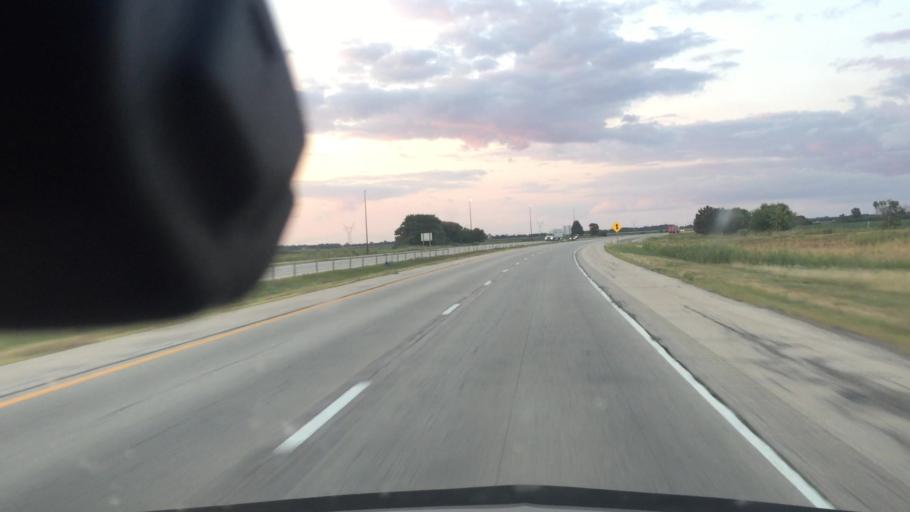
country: US
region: Illinois
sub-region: Grundy County
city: Gardner
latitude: 41.1875
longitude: -88.3212
